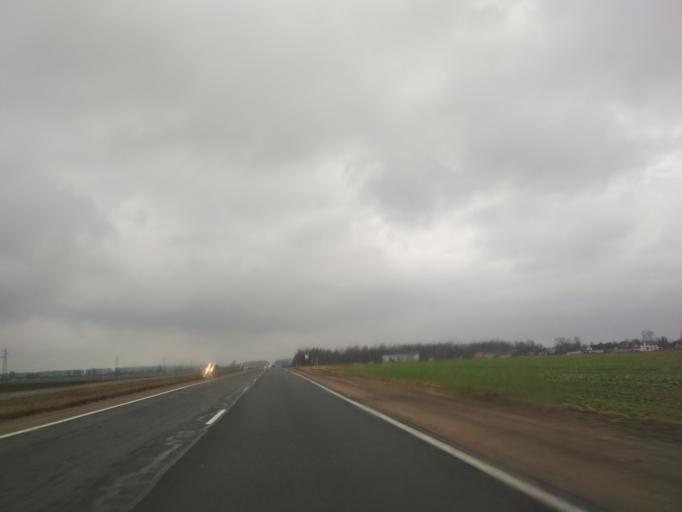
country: BY
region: Minsk
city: Dukora
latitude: 53.6392
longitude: 28.0013
